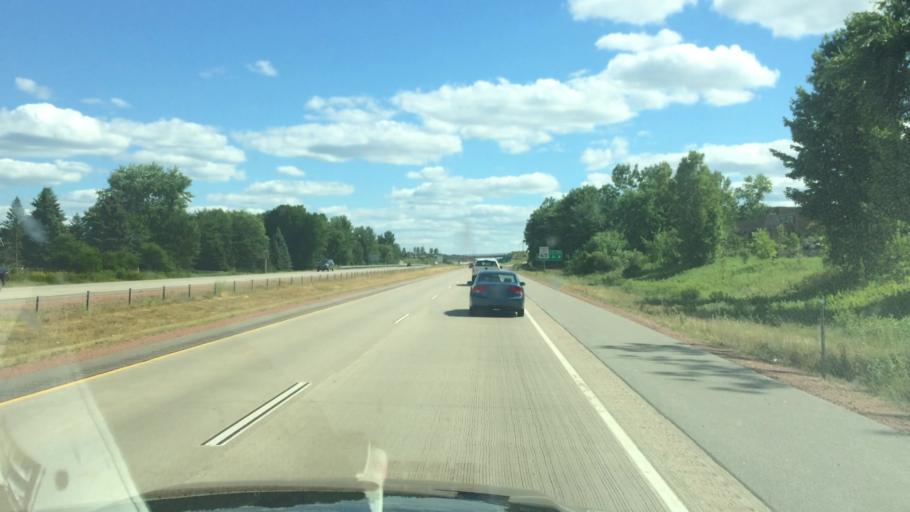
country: US
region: Wisconsin
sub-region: Marathon County
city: Wausau
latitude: 44.9774
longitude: -89.6573
